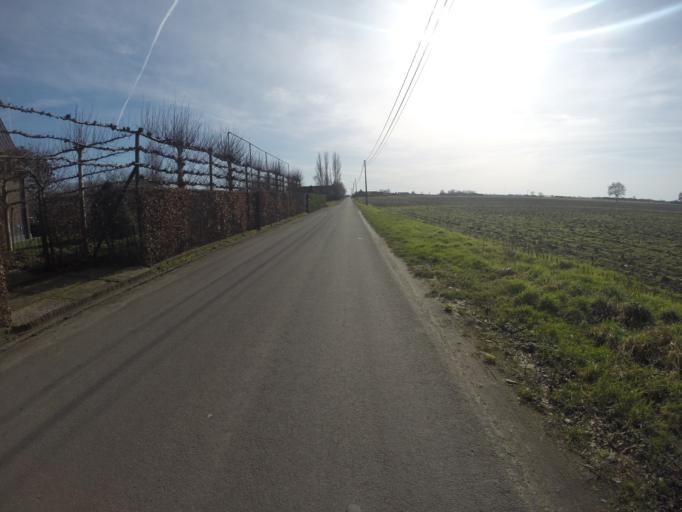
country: BE
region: Flanders
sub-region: Provincie West-Vlaanderen
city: Wingene
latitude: 51.0955
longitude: 3.2638
